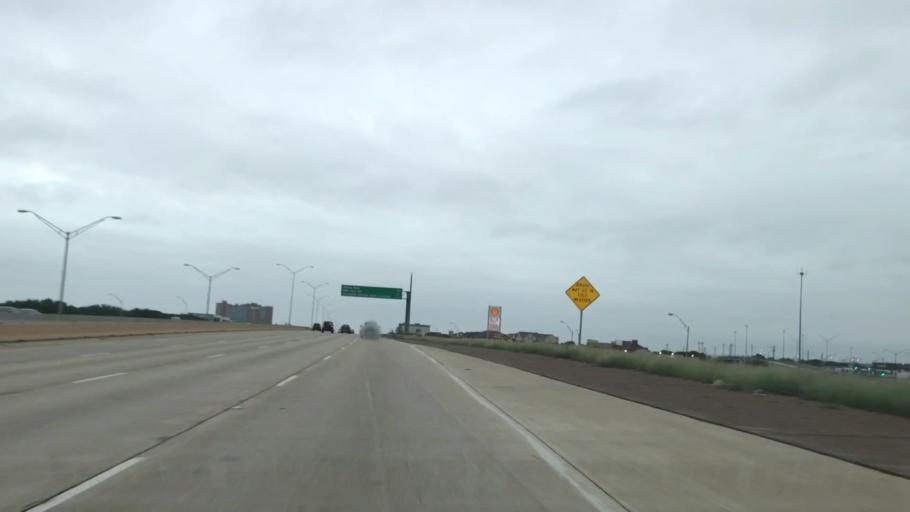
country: US
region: Texas
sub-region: Dallas County
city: Coppell
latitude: 32.9223
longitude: -97.0228
